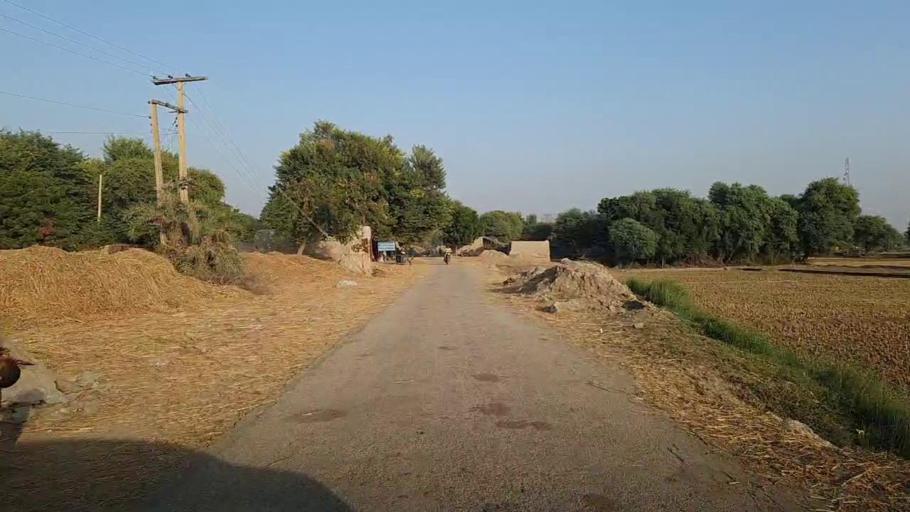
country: PK
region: Sindh
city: Kashmor
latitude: 28.4280
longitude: 69.4687
